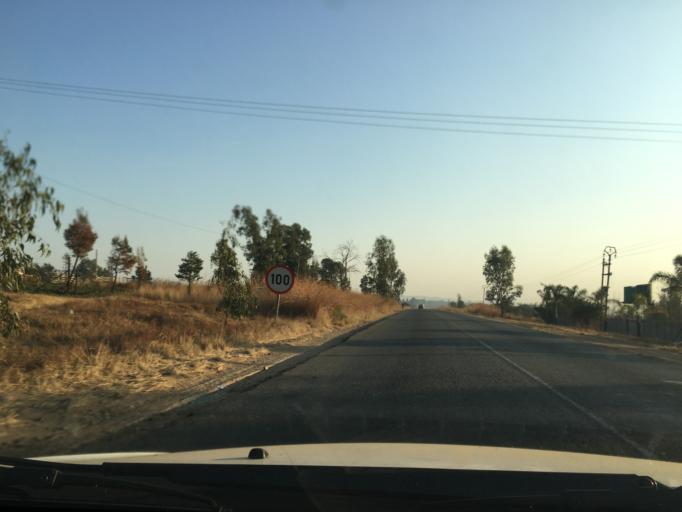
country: ZA
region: Gauteng
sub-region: West Rand District Municipality
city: Muldersdriseloop
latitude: -26.0129
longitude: 27.8587
